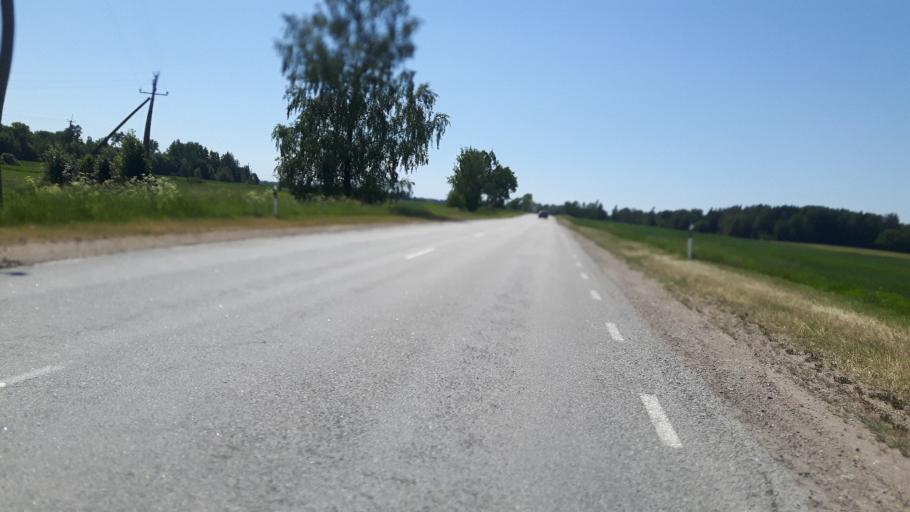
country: EE
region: Paernumaa
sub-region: Sindi linn
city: Sindi
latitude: 58.4462
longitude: 24.7638
